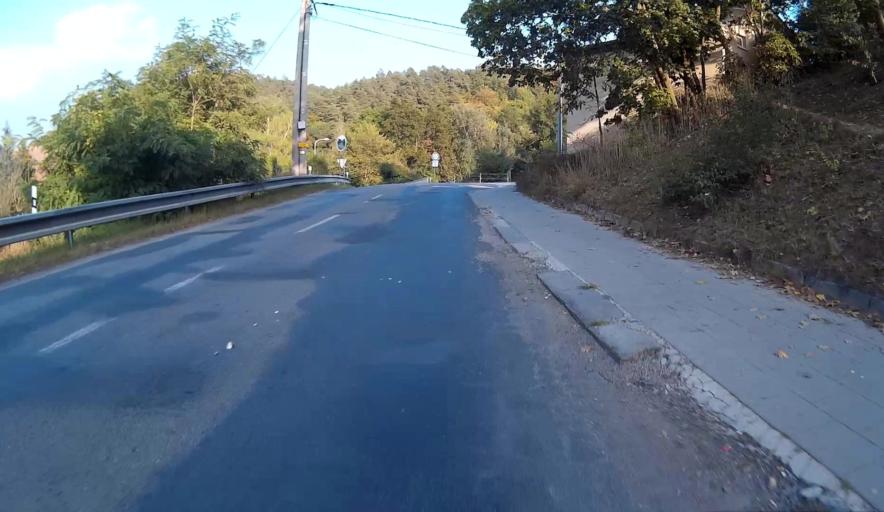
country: CZ
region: South Moravian
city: Podoli
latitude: 49.2029
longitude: 16.7146
